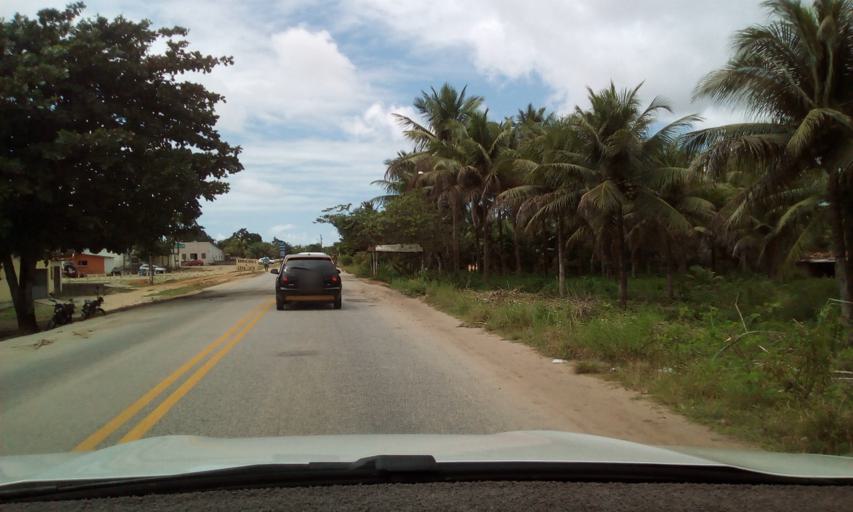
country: BR
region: Paraiba
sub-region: Rio Tinto
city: Rio Tinto
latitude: -6.7713
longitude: -35.0130
